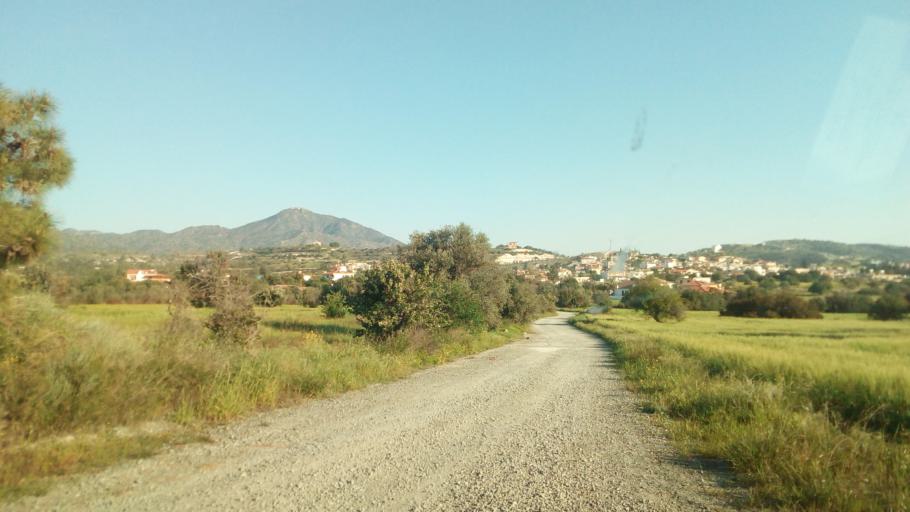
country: CY
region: Larnaka
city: Kofinou
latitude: 34.8471
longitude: 33.4528
